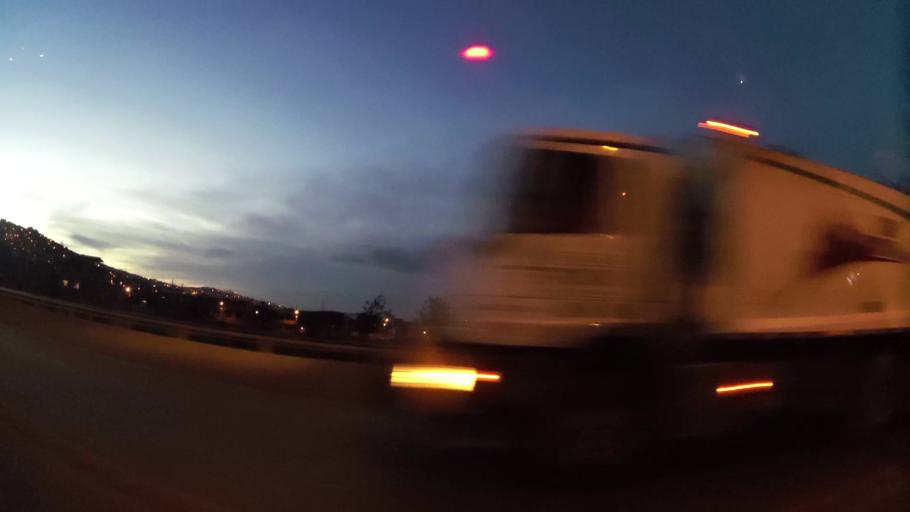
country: CO
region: Bogota D.C.
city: Bogota
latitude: 4.5592
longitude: -74.1340
